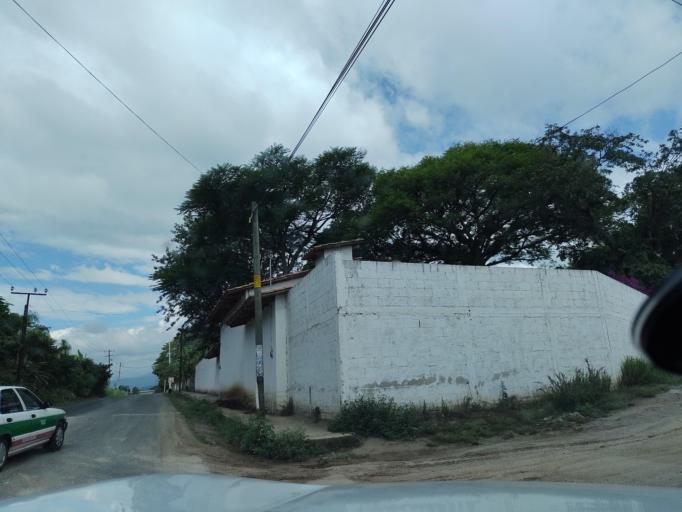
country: MX
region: Veracruz
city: Coatepec
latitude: 19.4815
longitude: -96.9363
